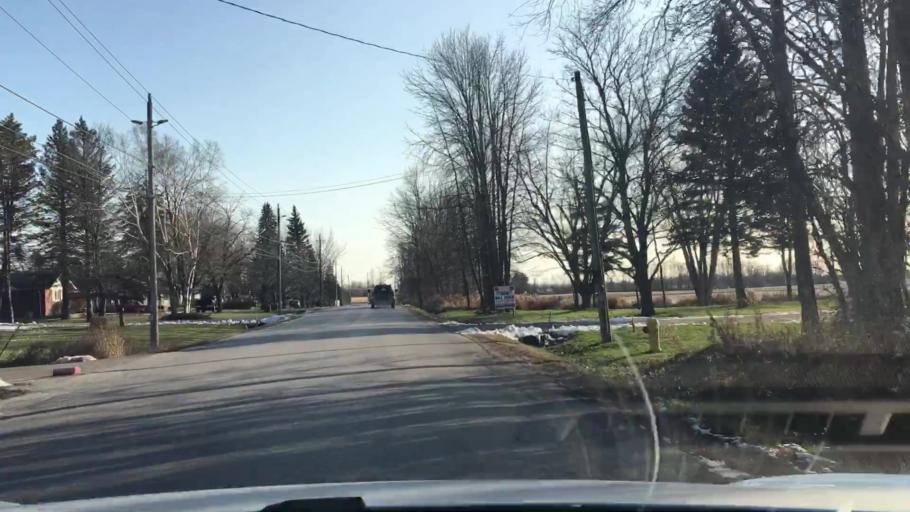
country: CA
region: Ontario
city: Oshawa
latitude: 43.8979
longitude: -78.7825
